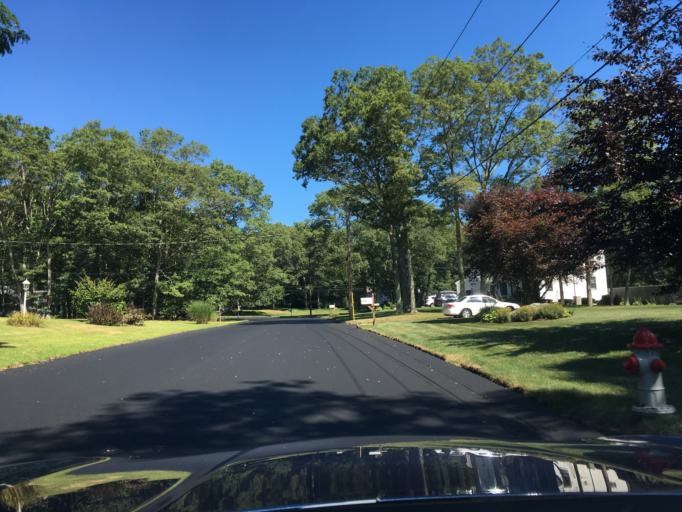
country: US
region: Rhode Island
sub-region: Kent County
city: East Greenwich
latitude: 41.6367
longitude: -71.4710
